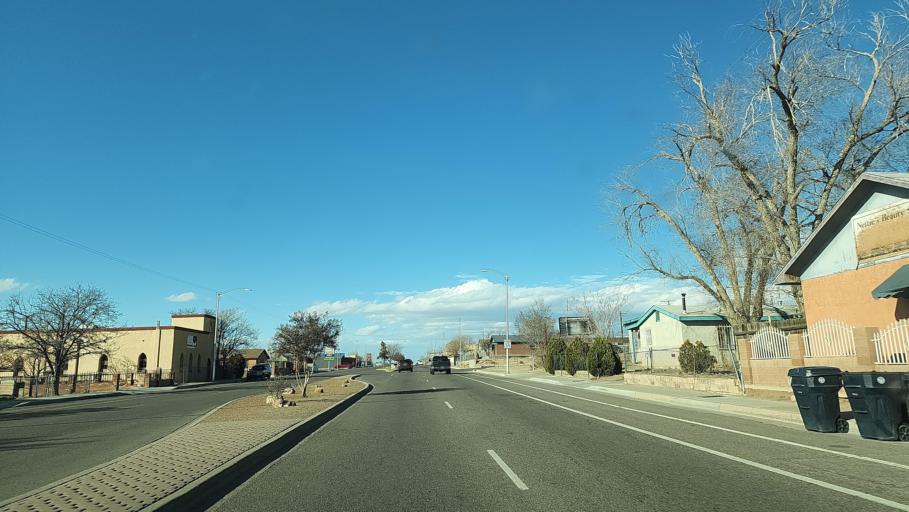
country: US
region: New Mexico
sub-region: Bernalillo County
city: Albuquerque
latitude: 35.0659
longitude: -106.6454
